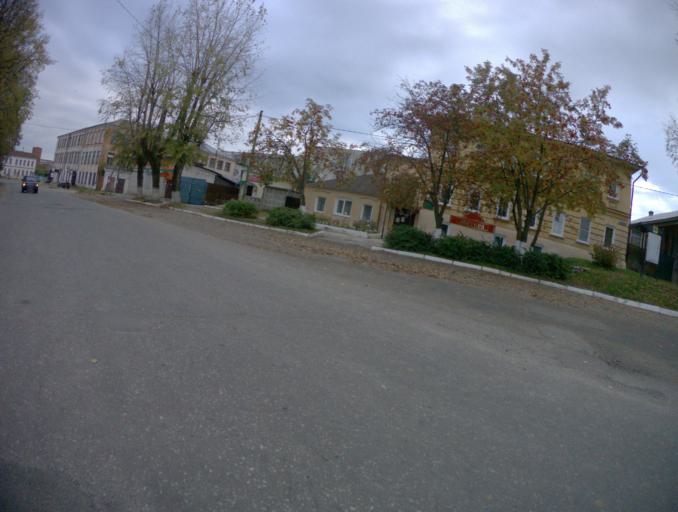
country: RU
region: Vladimir
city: Mstera
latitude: 56.3741
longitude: 41.9400
